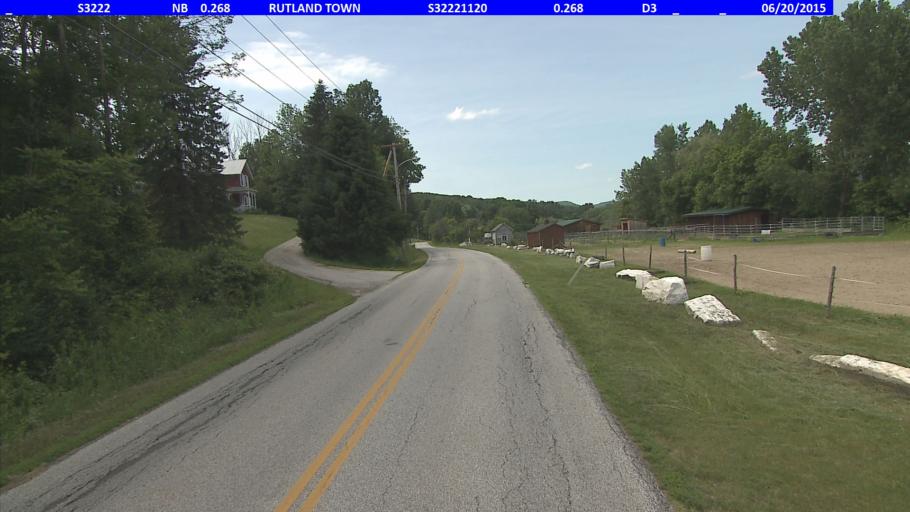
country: US
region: Vermont
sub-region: Rutland County
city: West Rutland
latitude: 43.6030
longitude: -73.0225
